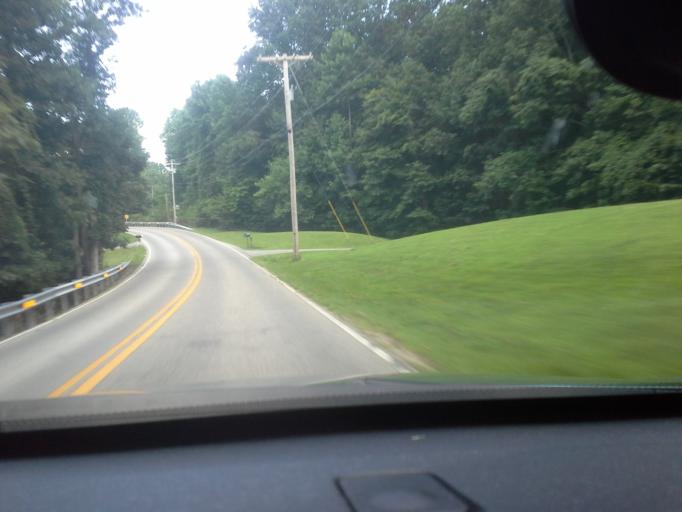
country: US
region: Maryland
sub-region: Calvert County
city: Prince Frederick
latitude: 38.5927
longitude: -76.5441
